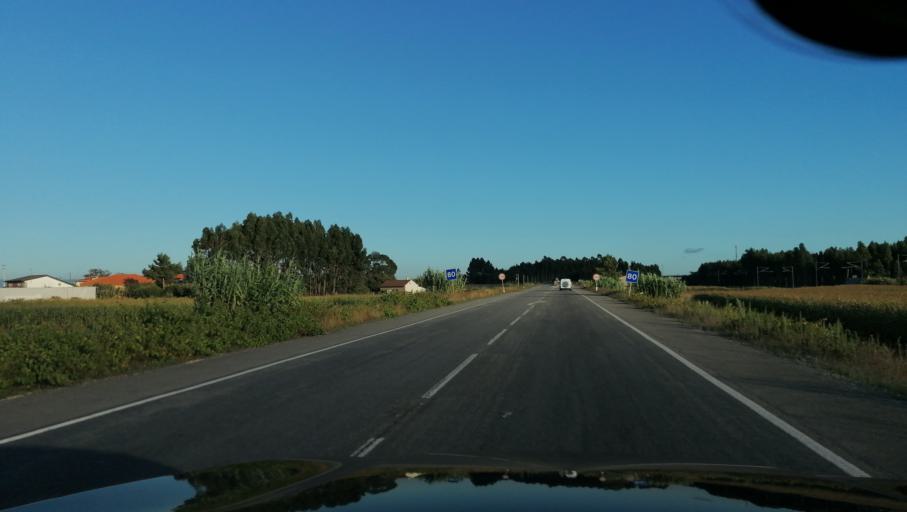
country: PT
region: Aveiro
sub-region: Aveiro
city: Oliveirinha
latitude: 40.6024
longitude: -8.6189
